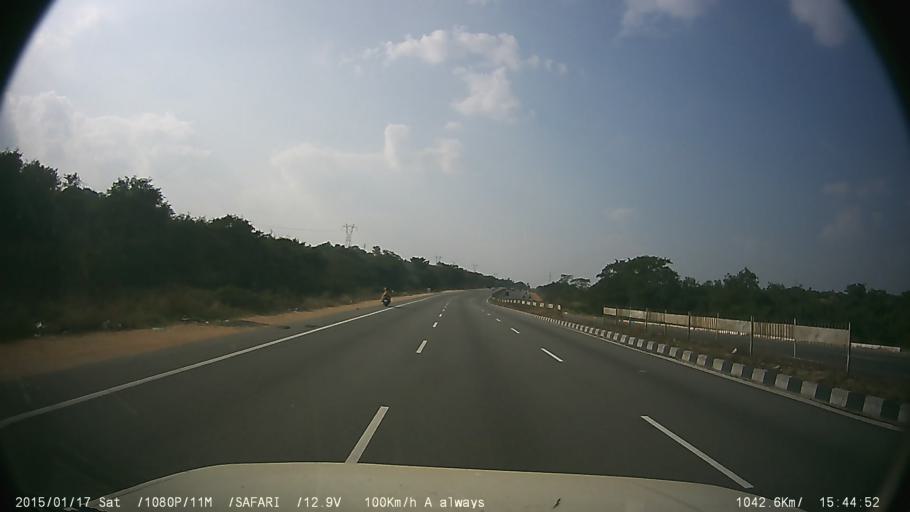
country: IN
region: Tamil Nadu
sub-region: Krishnagiri
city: Hosur
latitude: 12.7013
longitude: 77.9085
